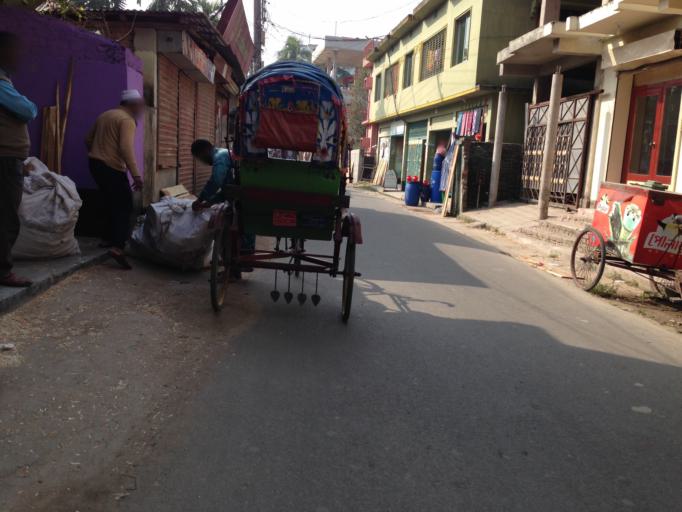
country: BD
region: Chittagong
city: Lakshmipur
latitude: 22.9370
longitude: 90.8314
